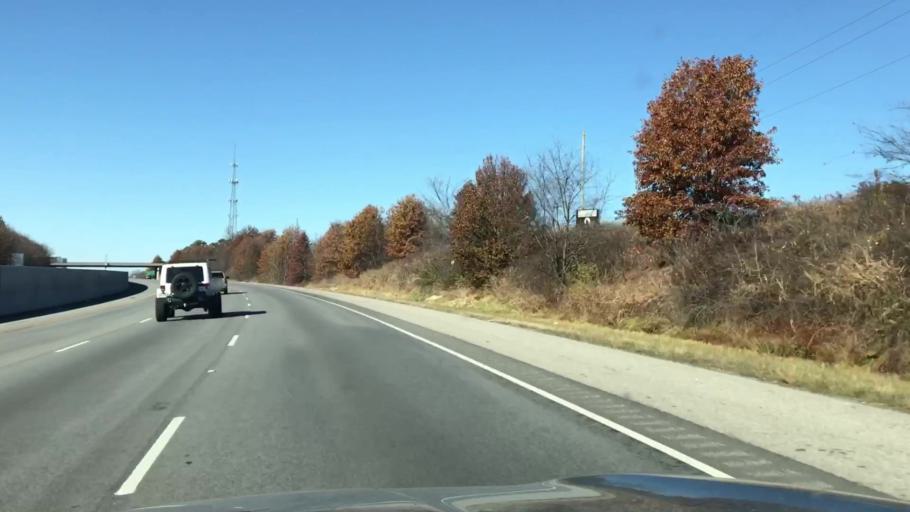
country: US
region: Arkansas
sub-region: Benton County
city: Lowell
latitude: 36.2955
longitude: -94.1666
